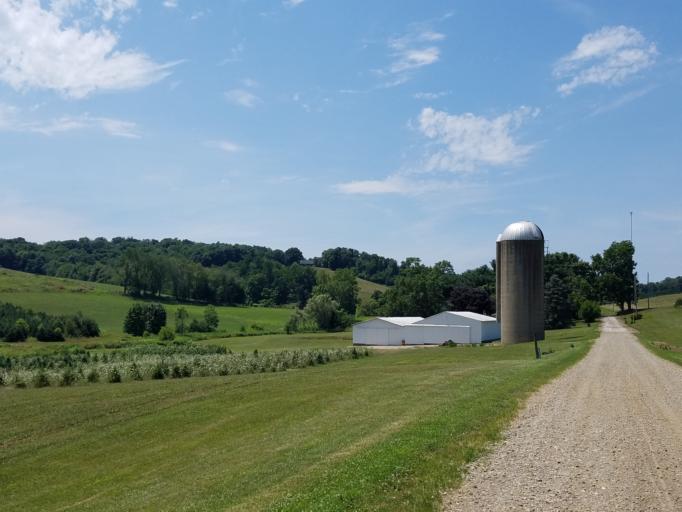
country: US
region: Ohio
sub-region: Knox County
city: Danville
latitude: 40.5146
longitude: -82.3305
